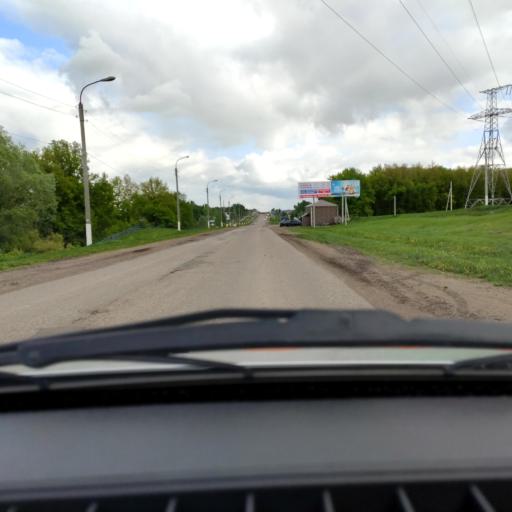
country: RU
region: Bashkortostan
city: Tolbazy
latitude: 54.0028
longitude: 55.8981
